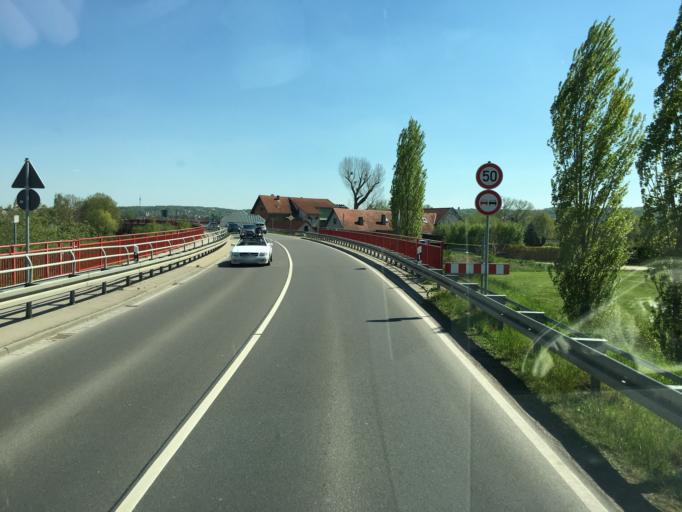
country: DE
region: Saxony-Anhalt
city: Naumburg
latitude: 51.1682
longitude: 11.7813
